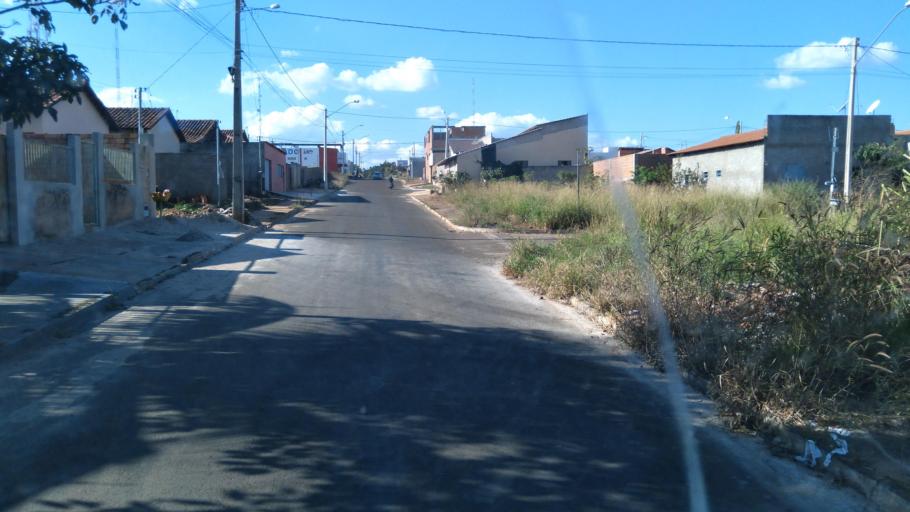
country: BR
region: Goias
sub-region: Mineiros
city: Mineiros
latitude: -17.5470
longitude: -52.5384
